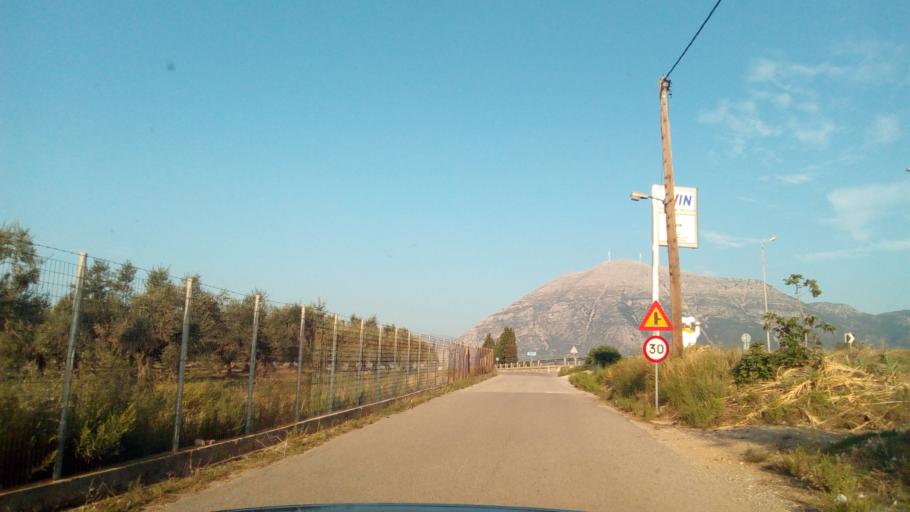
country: GR
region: West Greece
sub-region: Nomos Aitolias kai Akarnanias
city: Antirrio
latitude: 38.3375
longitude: 21.7444
